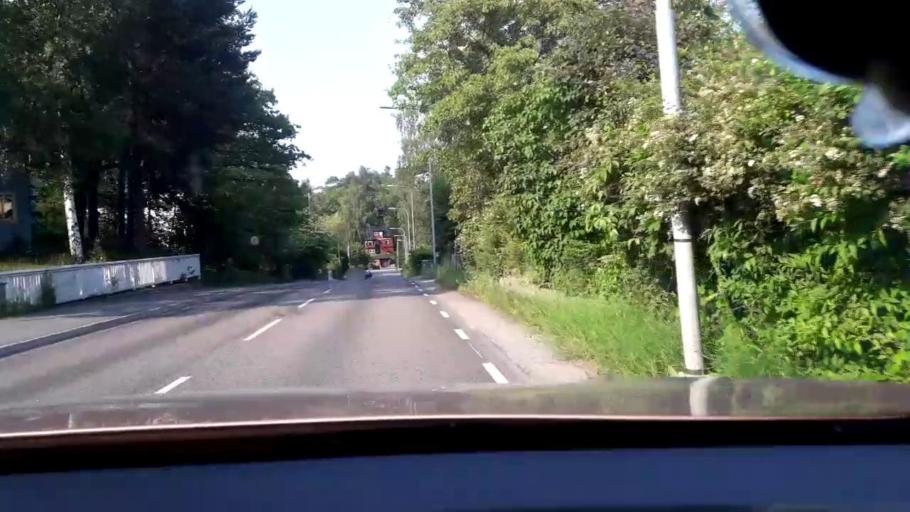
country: SE
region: Stockholm
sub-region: Lidingo
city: Brevik
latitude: 59.3180
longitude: 18.2044
